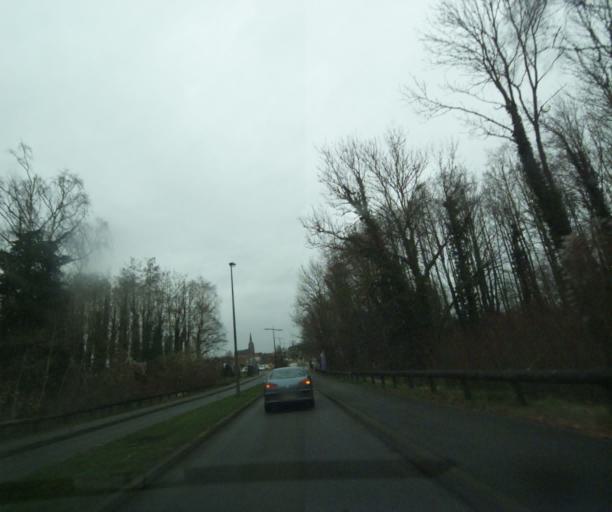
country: FR
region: Nord-Pas-de-Calais
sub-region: Departement du Nord
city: Fresnes-sur-Escaut
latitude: 50.4276
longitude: 3.5800
